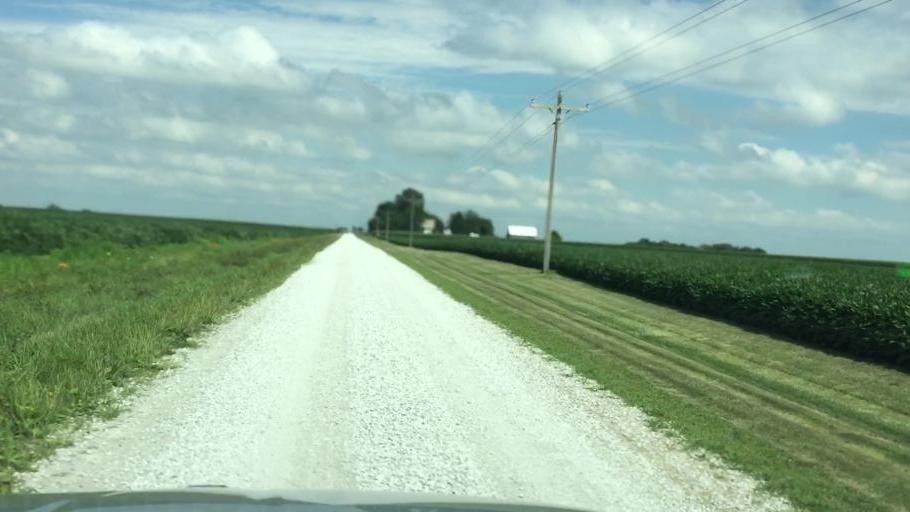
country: US
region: Illinois
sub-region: Hancock County
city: Nauvoo
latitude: 40.5217
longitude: -91.2966
